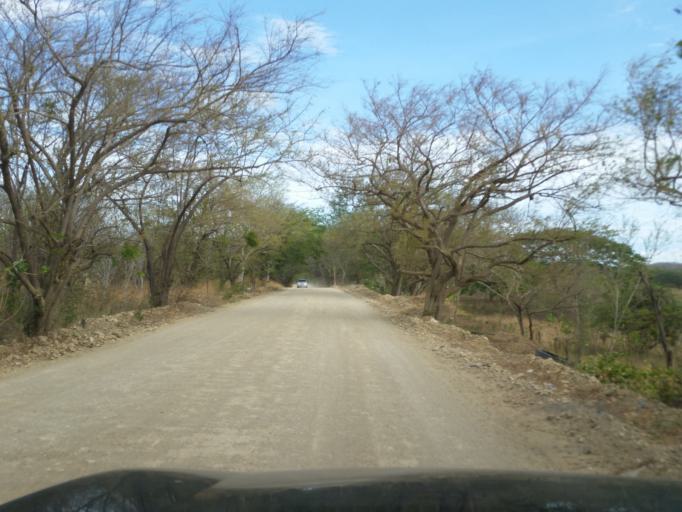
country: NI
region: Rivas
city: Tola
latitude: 11.4259
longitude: -86.0130
